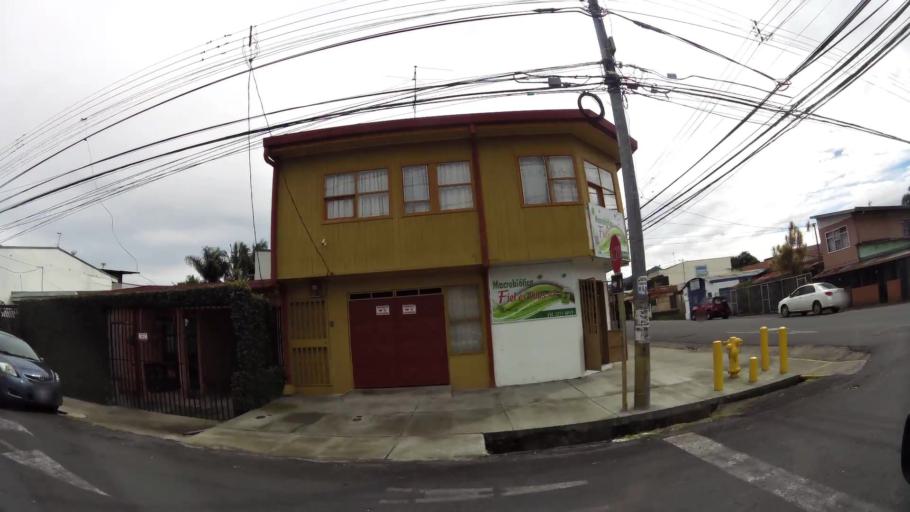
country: CR
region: San Jose
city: Curridabat
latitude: 9.9142
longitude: -84.0392
